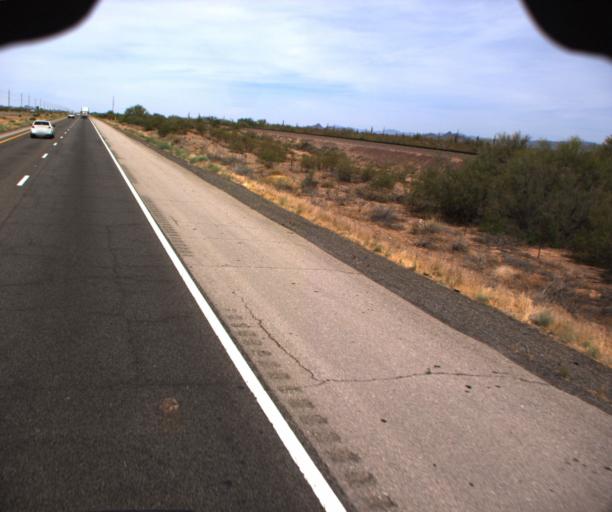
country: US
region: Arizona
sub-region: Maricopa County
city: Wickenburg
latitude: 33.8000
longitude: -112.5568
